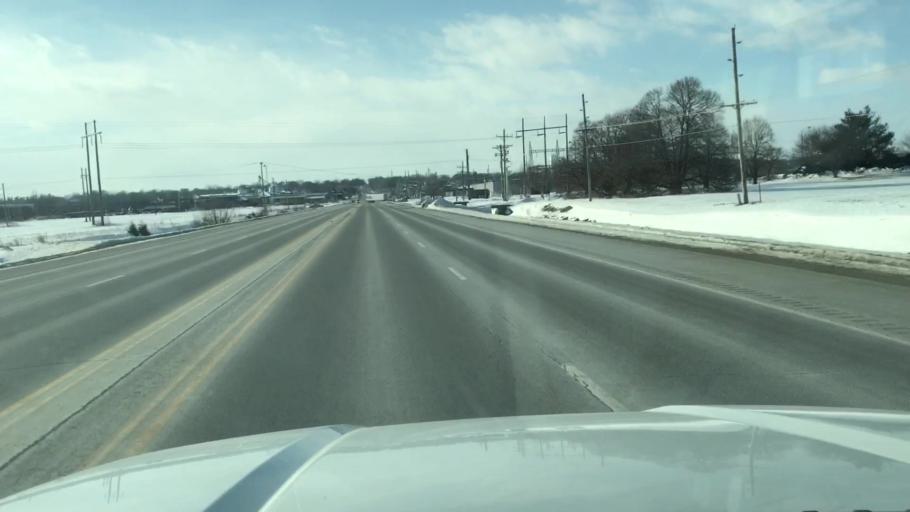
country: US
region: Missouri
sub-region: Nodaway County
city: Maryville
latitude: 40.3451
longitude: -94.8398
